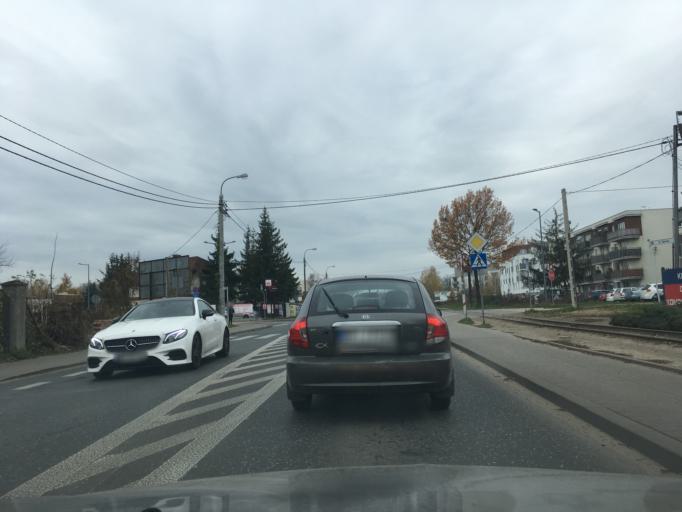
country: PL
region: Masovian Voivodeship
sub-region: Powiat piaseczynski
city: Piaseczno
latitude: 52.0678
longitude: 21.0229
